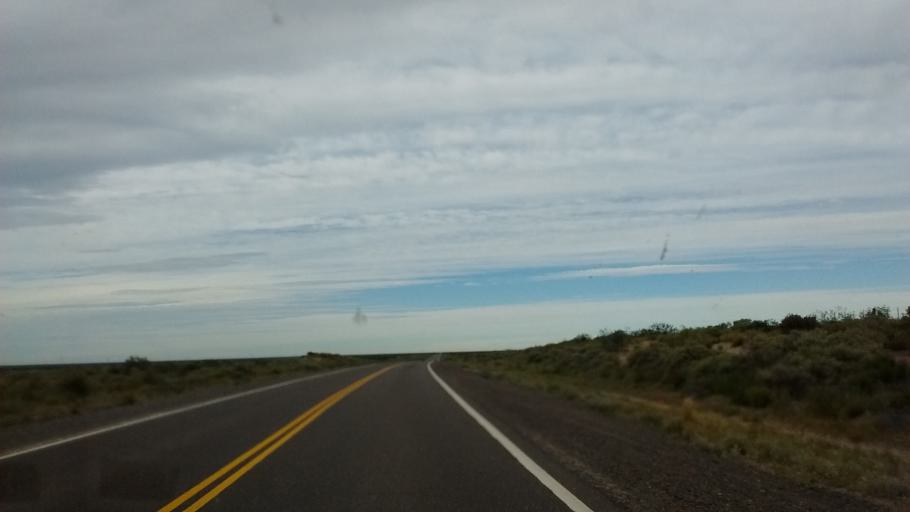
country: AR
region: Rio Negro
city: Contraalmirante Cordero
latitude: -38.4656
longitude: -68.0478
